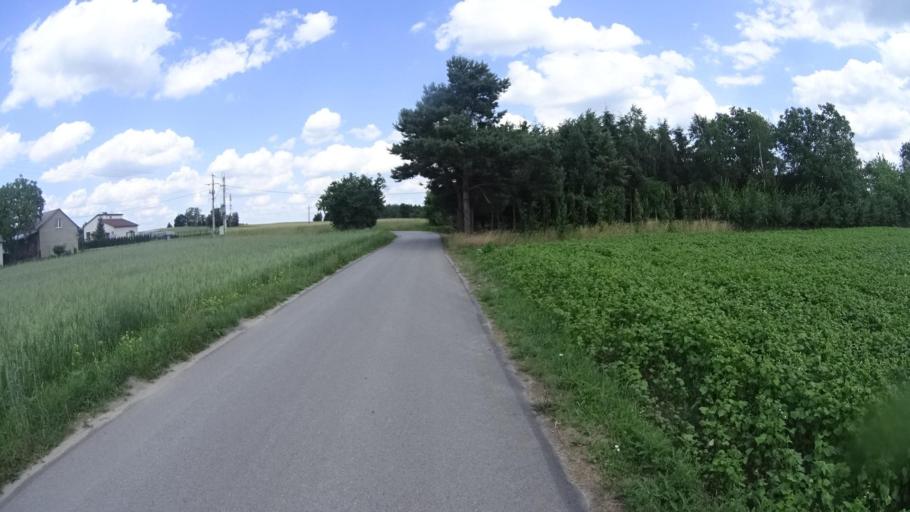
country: PL
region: Masovian Voivodeship
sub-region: Powiat bialobrzeski
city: Promna
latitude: 51.7063
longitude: 20.9199
